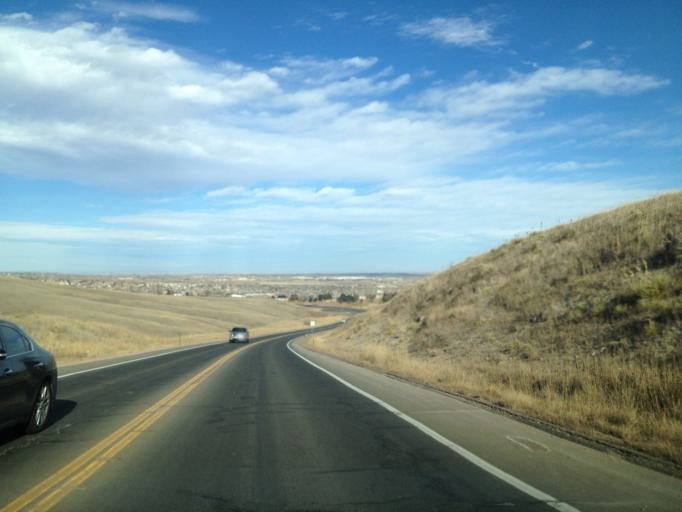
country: US
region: Colorado
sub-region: Boulder County
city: Superior
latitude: 39.9116
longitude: -105.1685
